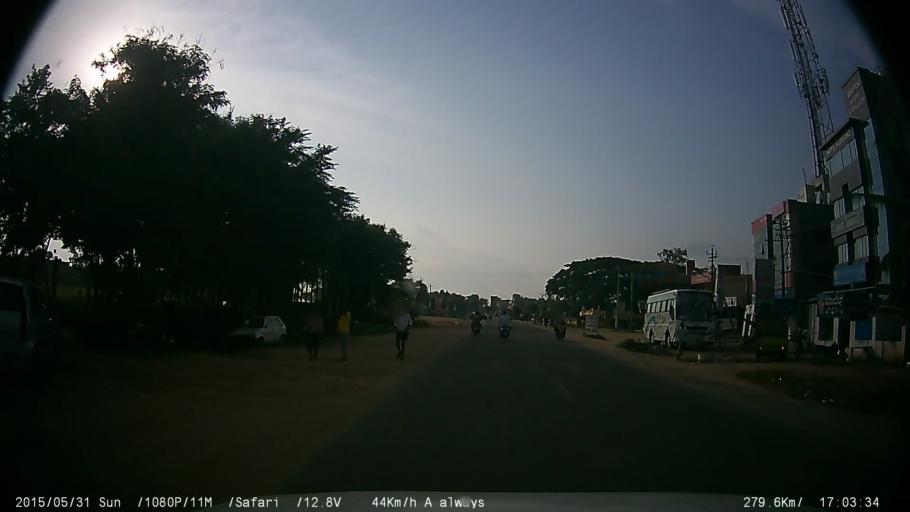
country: IN
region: Karnataka
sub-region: Chamrajnagar
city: Gundlupet
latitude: 11.8136
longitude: 76.6863
